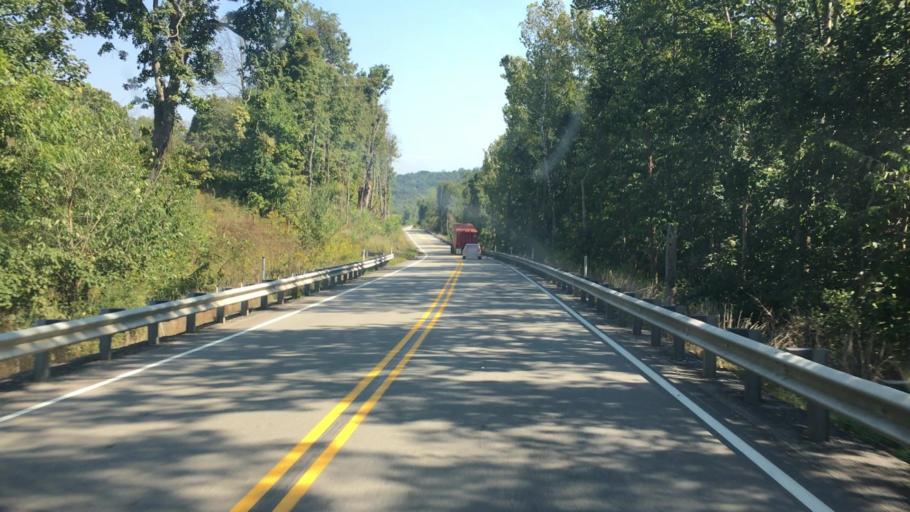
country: US
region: Pennsylvania
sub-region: Washington County
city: Washington
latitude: 40.0282
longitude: -80.3008
